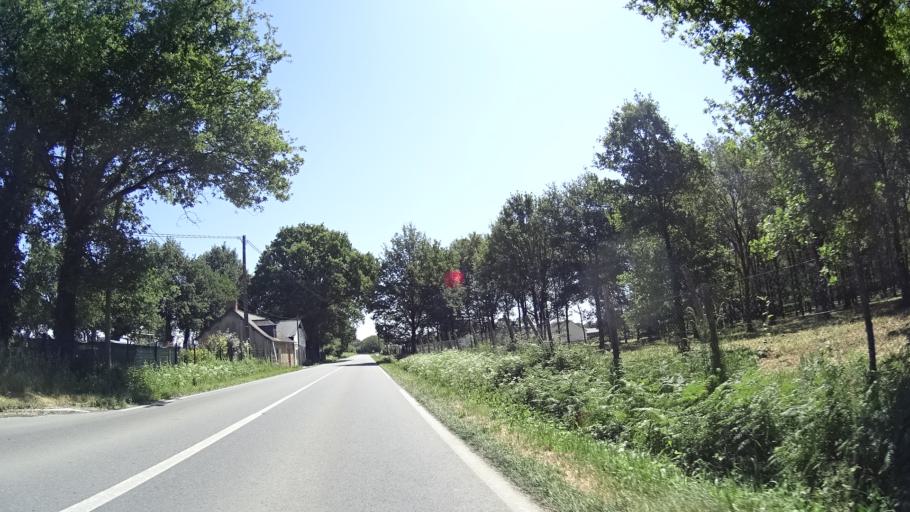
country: FR
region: Brittany
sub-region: Departement d'Ille-et-Vilaine
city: Messac
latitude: 47.8247
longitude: -1.7843
